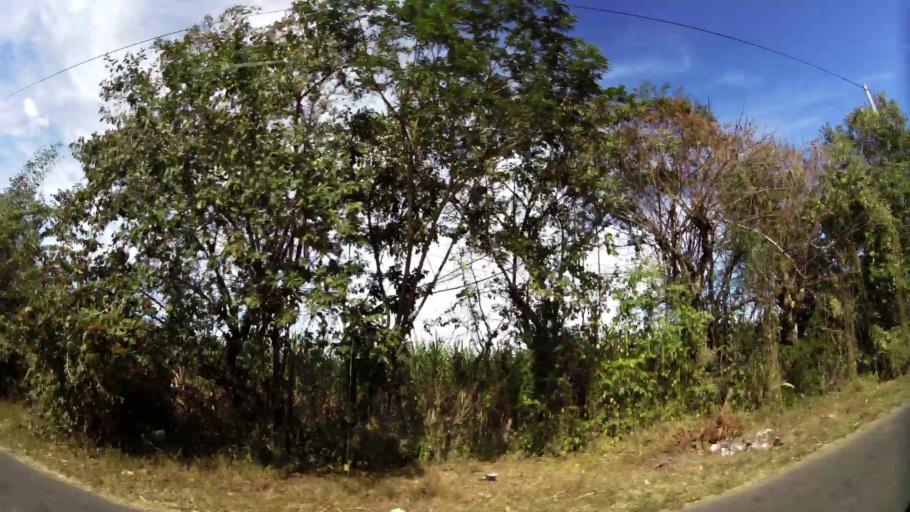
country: SV
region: San Salvador
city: Aguilares
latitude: 13.9625
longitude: -89.1111
